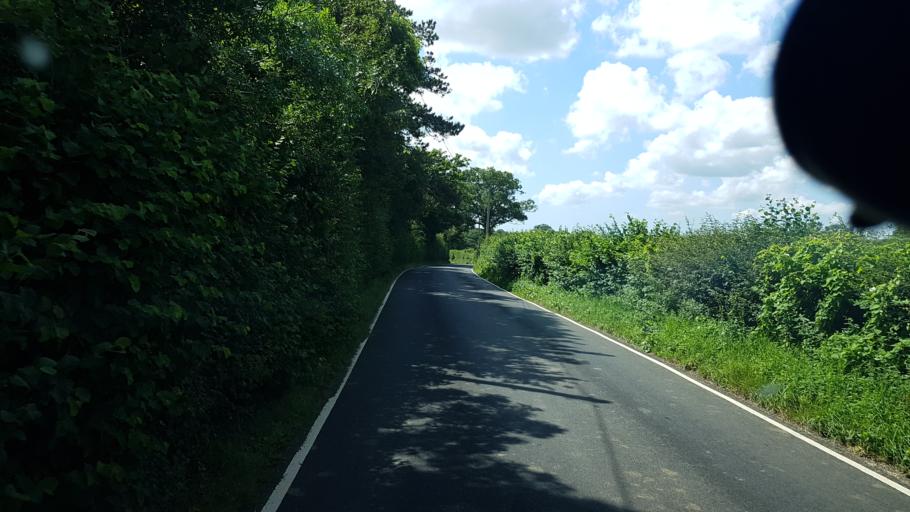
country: GB
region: England
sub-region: Kent
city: Edenbridge
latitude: 51.2105
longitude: 0.1288
